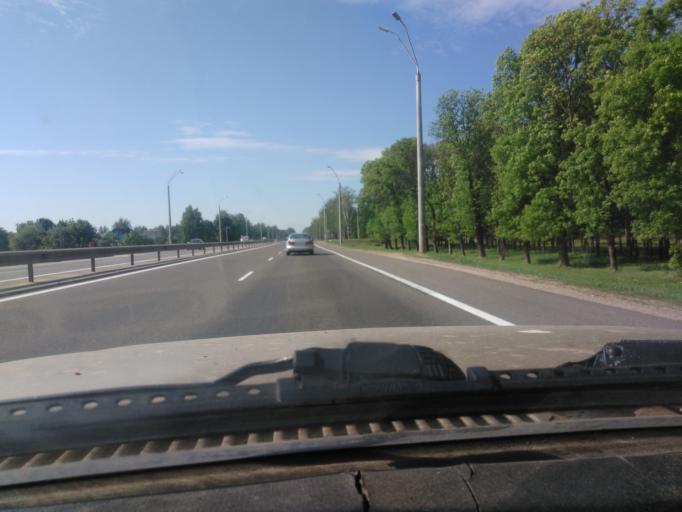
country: BY
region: Mogilev
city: Buynichy
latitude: 53.8572
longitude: 30.2559
